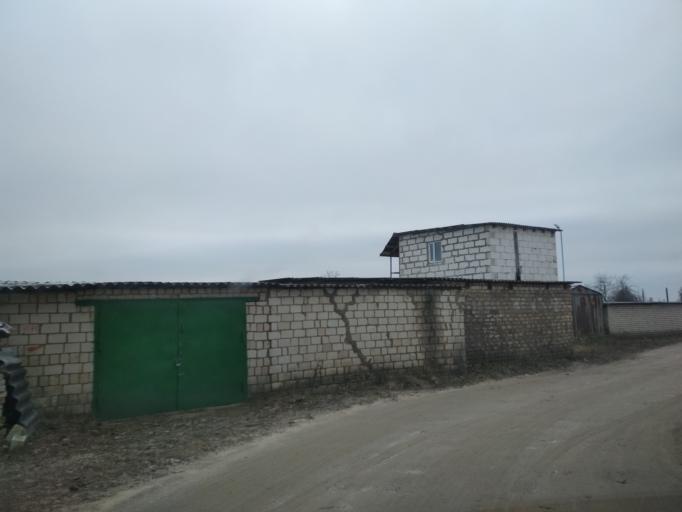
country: BY
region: Minsk
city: Mar''ina Horka
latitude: 53.5026
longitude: 28.1533
